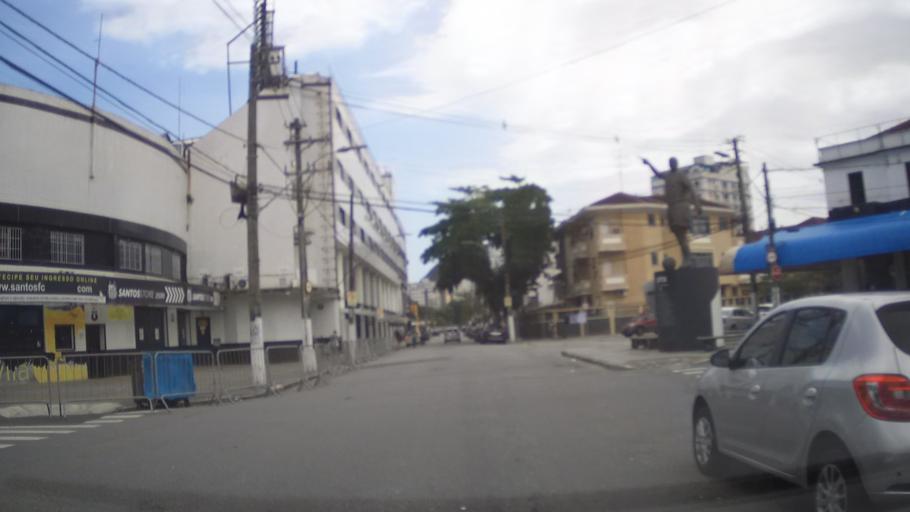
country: BR
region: Sao Paulo
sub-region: Santos
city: Santos
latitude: -23.9501
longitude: -46.3389
